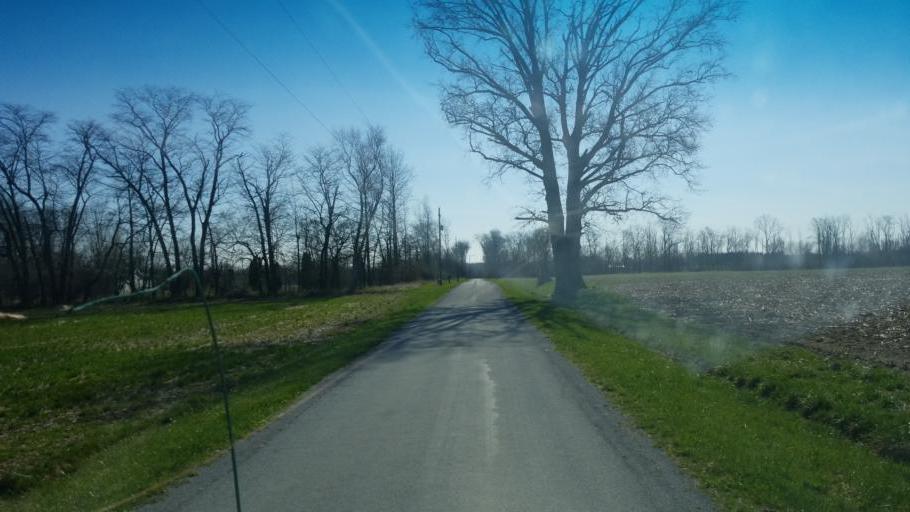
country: US
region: Ohio
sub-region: Hardin County
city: Forest
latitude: 40.7094
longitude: -83.4511
